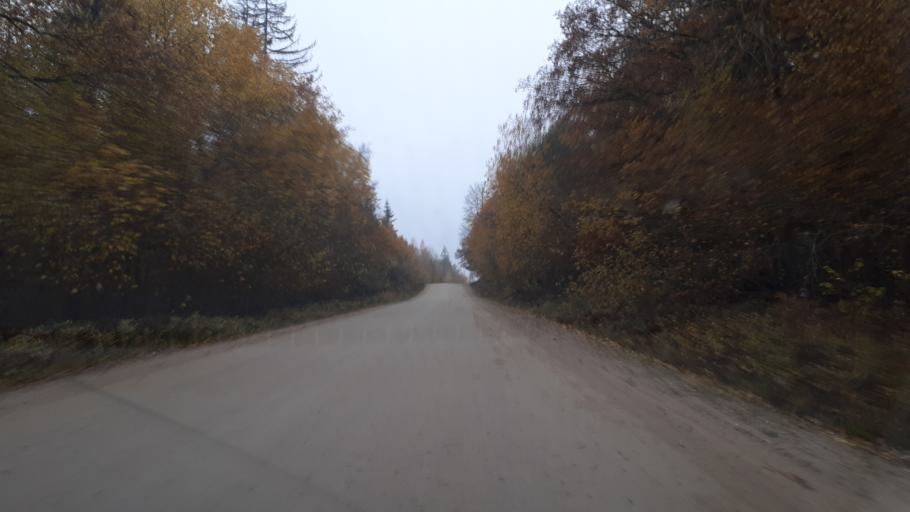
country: LV
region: Kuldigas Rajons
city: Kuldiga
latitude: 56.9488
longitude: 21.8521
